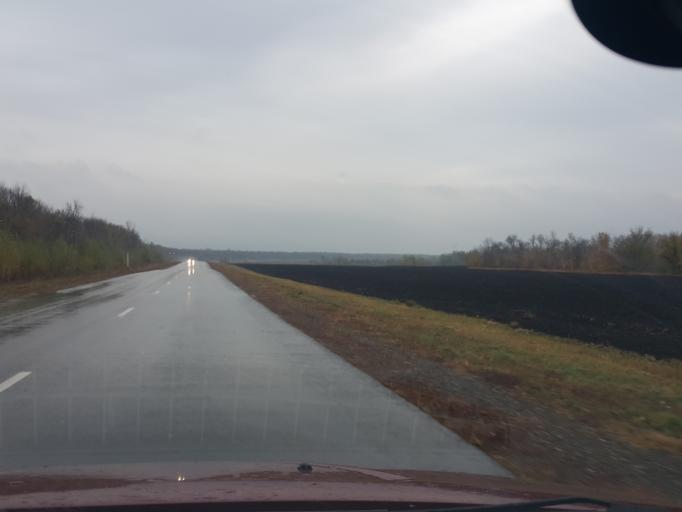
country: RU
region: Tambov
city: Znamenka
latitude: 52.4483
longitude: 41.4989
